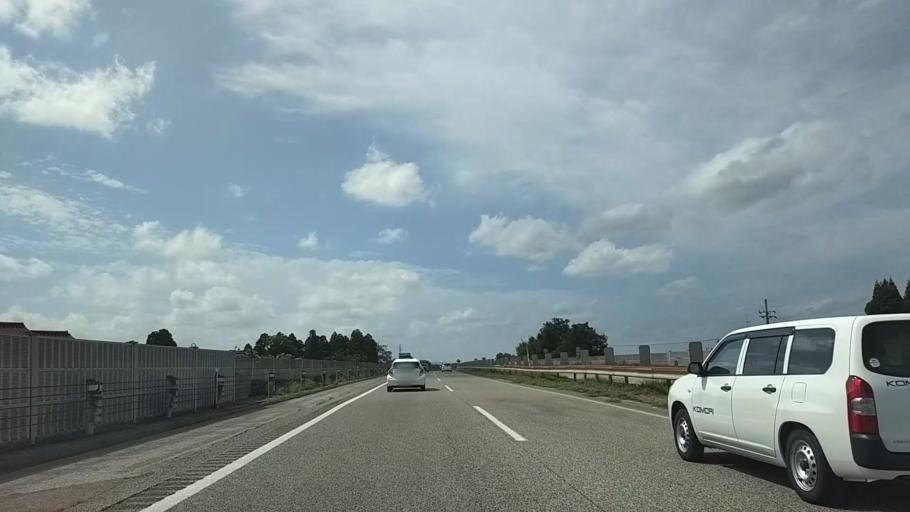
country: JP
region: Toyama
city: Takaoka
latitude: 36.6615
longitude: 137.0199
